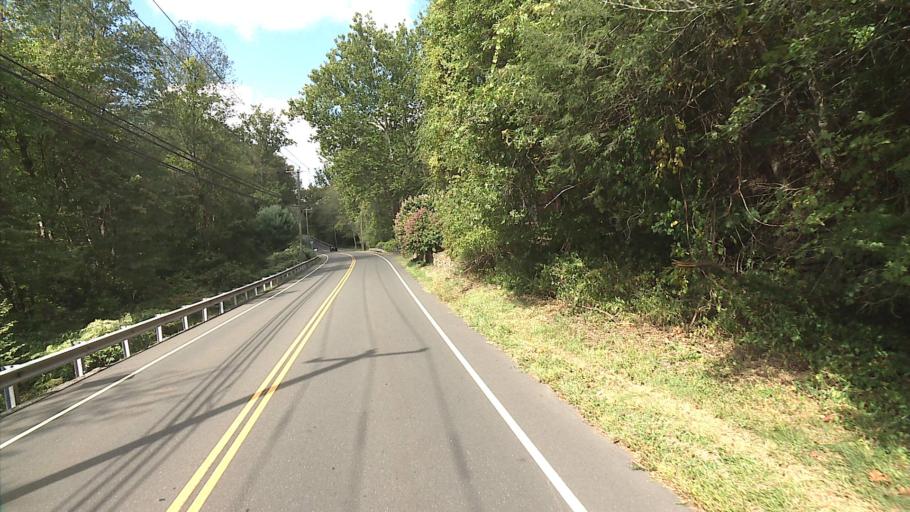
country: US
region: Connecticut
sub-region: Middlesex County
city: Chester Center
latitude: 41.3991
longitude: -72.4844
